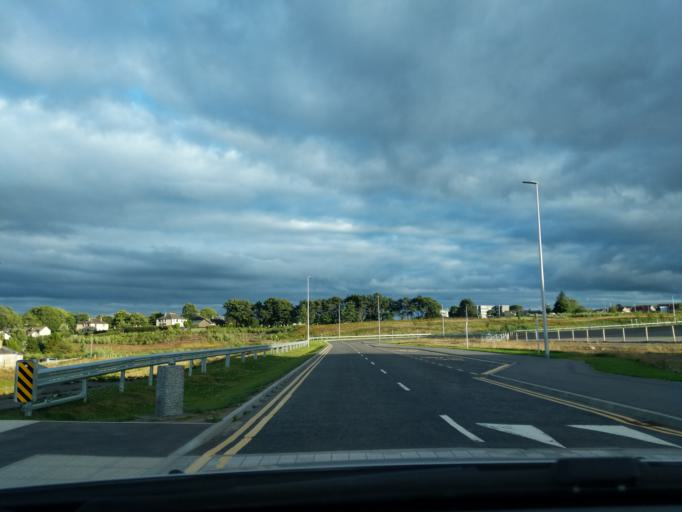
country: GB
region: Scotland
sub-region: Aberdeen City
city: Dyce
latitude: 57.1856
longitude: -2.1872
